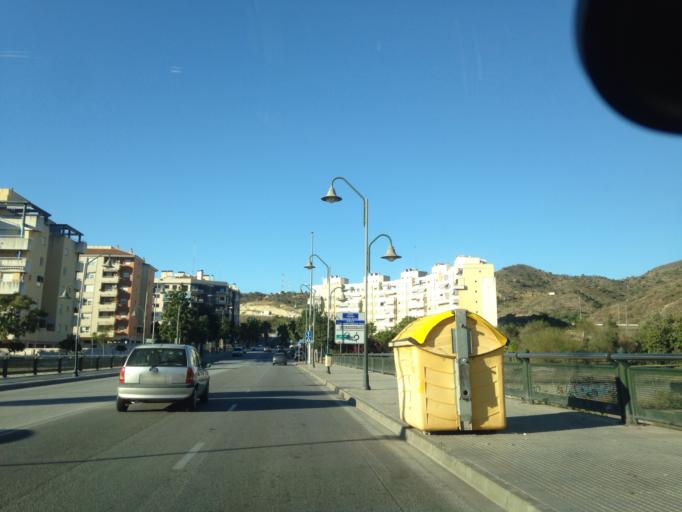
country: ES
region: Andalusia
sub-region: Provincia de Malaga
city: Malaga
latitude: 36.7530
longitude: -4.4267
